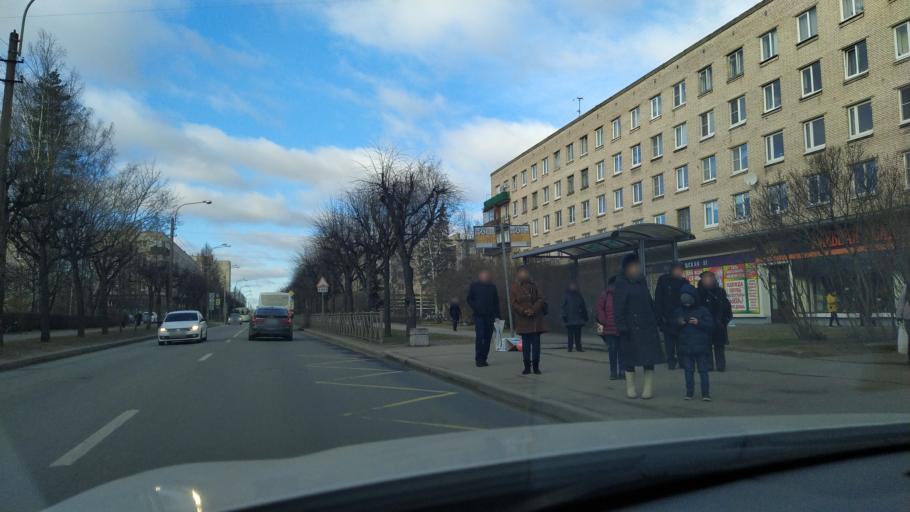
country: RU
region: St.-Petersburg
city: Pushkin
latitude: 59.7286
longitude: 30.4118
